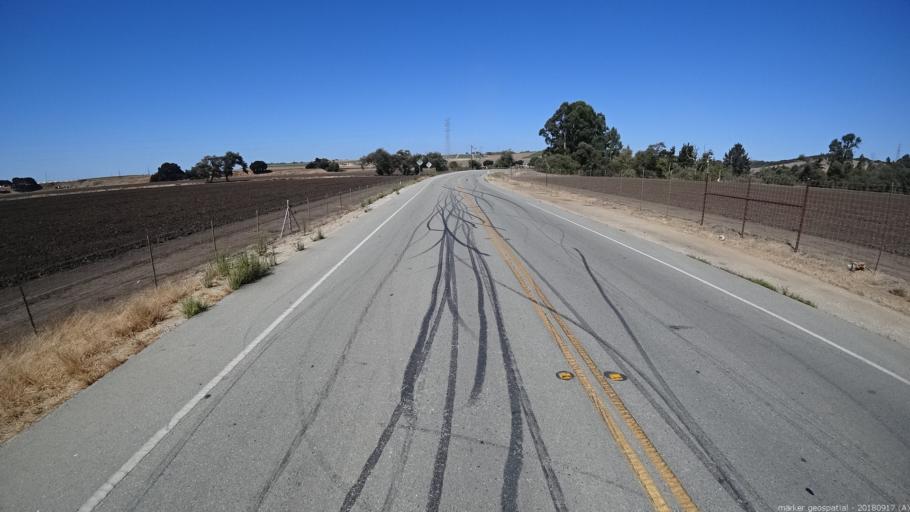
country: US
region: California
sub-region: Monterey County
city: Prunedale
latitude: 36.7704
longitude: -121.6007
